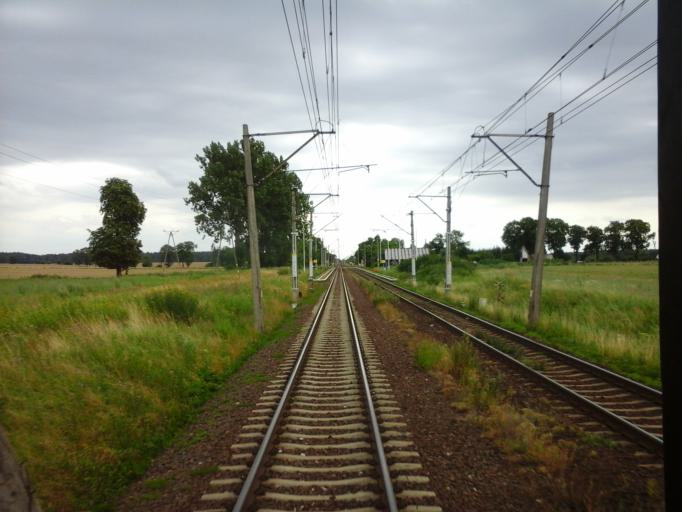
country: PL
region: West Pomeranian Voivodeship
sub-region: Powiat stargardzki
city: Dolice
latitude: 53.2206
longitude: 15.1523
